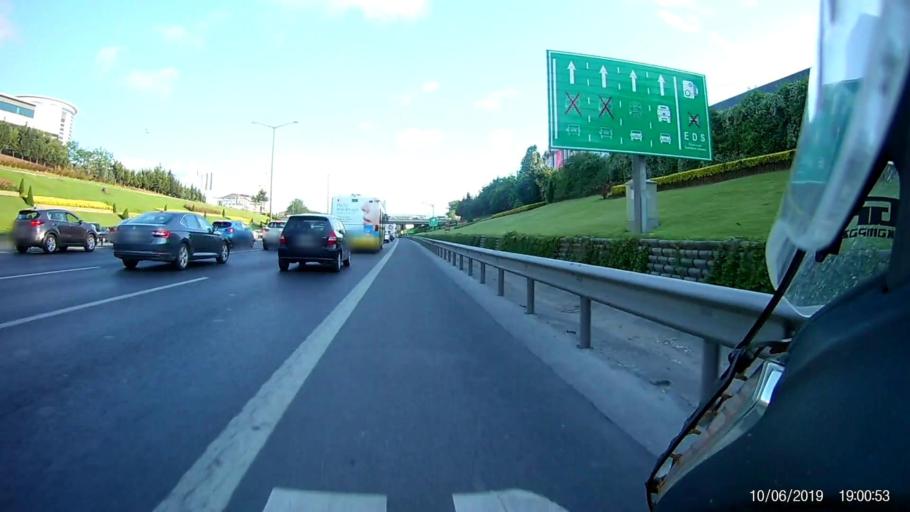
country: TR
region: Istanbul
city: Sancaktepe
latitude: 41.0314
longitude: 29.2577
